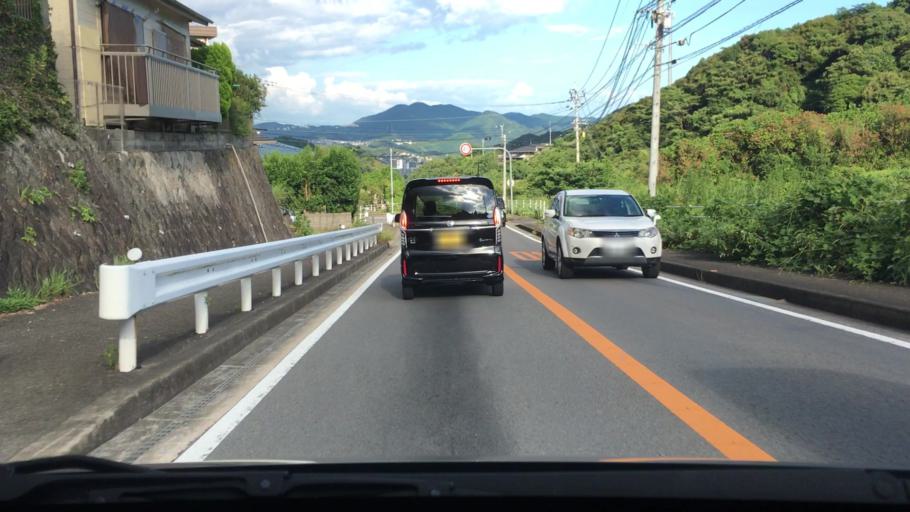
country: JP
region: Nagasaki
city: Togitsu
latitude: 32.8108
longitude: 129.8217
